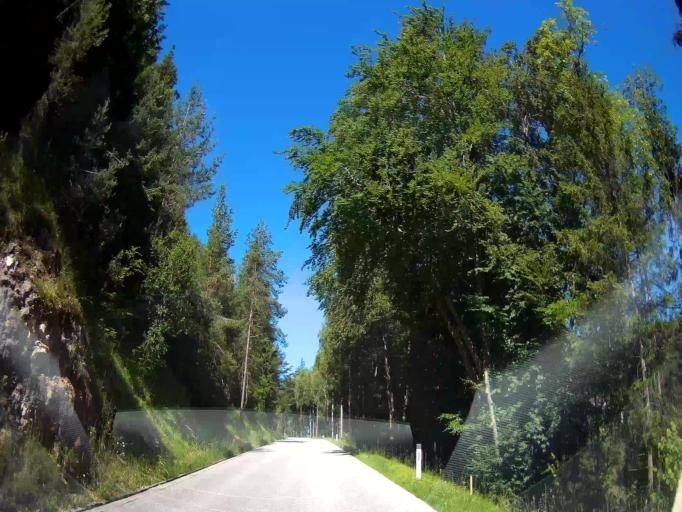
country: AT
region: Carinthia
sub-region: Politischer Bezirk Klagenfurt Land
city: Maria Worth
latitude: 46.6021
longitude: 14.1485
